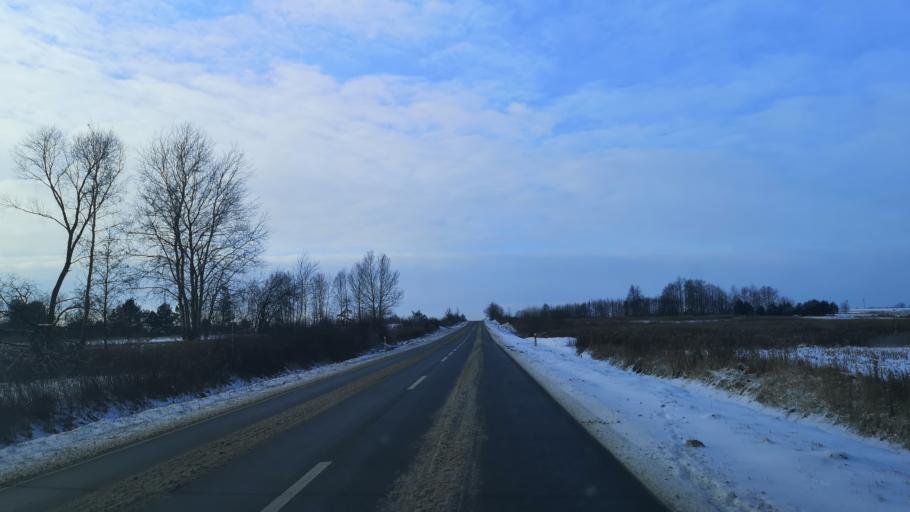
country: PL
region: Subcarpathian Voivodeship
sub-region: Powiat przeworski
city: Sieniawa
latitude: 50.1989
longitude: 22.6303
